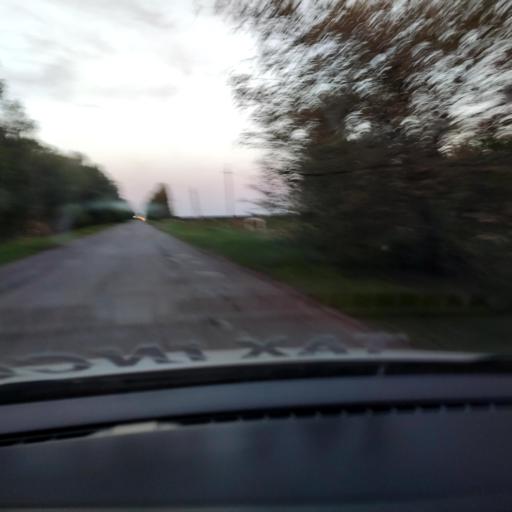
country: RU
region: Voronezj
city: Maslovka
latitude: 51.4438
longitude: 39.2617
